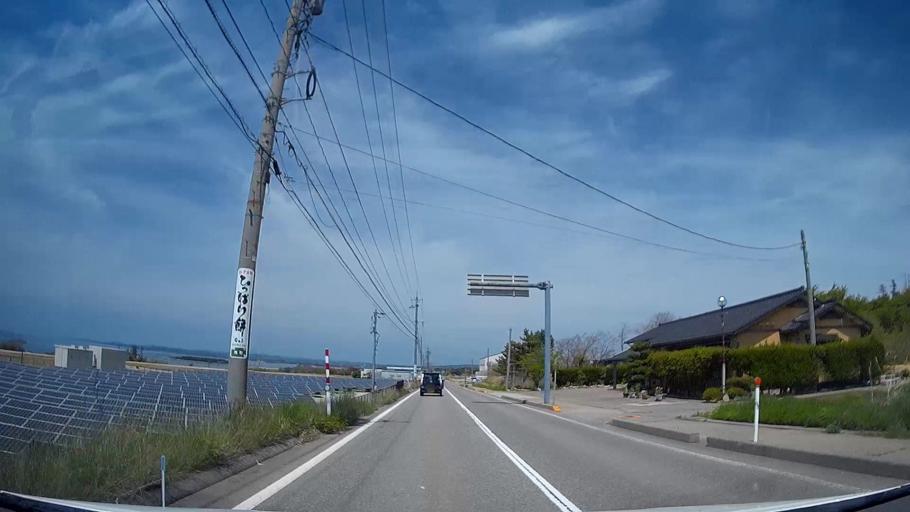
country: JP
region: Ishikawa
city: Hakui
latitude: 36.9345
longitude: 136.7573
